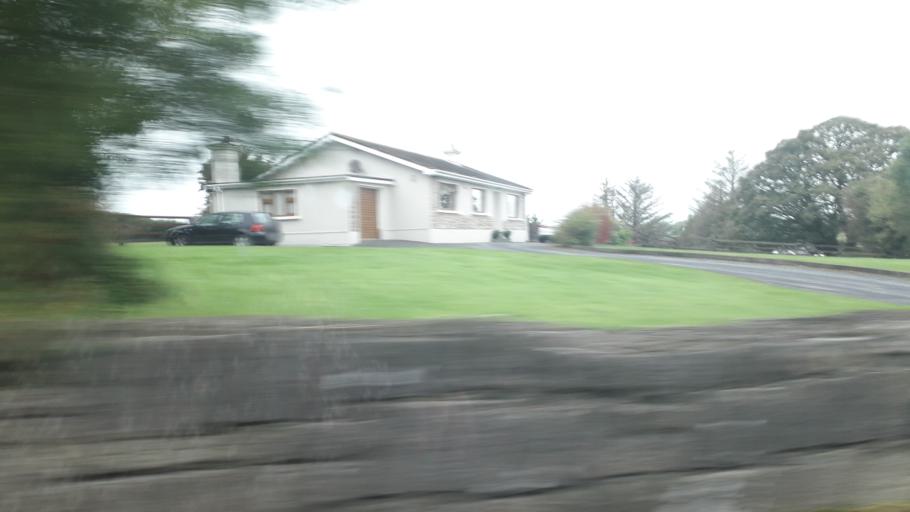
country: IE
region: Leinster
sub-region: An Longfort
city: Lanesborough
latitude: 53.7709
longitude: -8.1031
